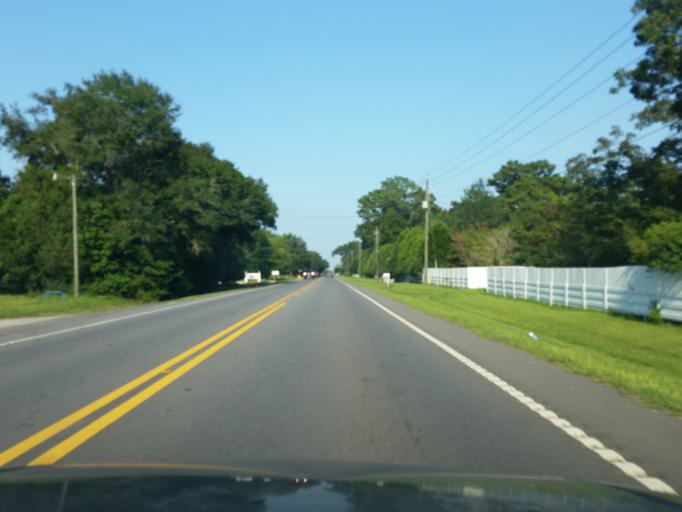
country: US
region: Alabama
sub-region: Baldwin County
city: Foley
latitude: 30.4066
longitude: -87.7111
